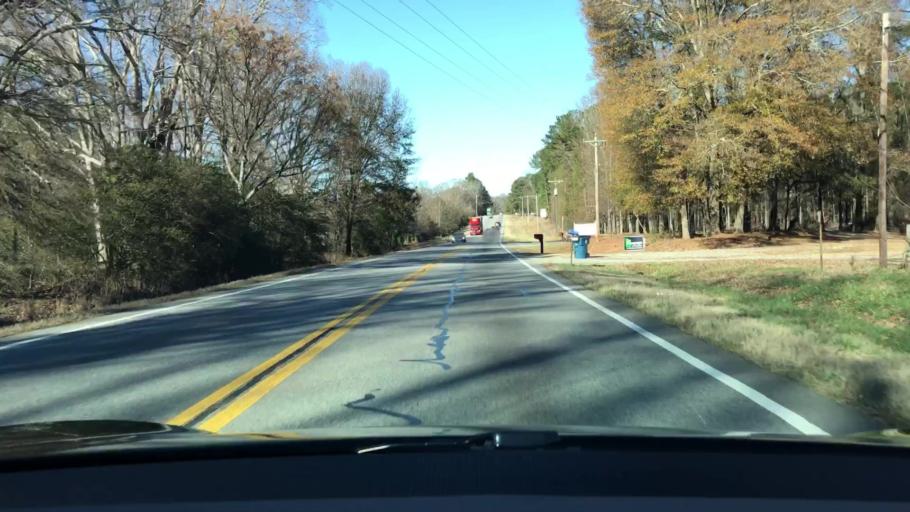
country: US
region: Georgia
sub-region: Walton County
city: Monroe
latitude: 33.8848
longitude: -83.7212
